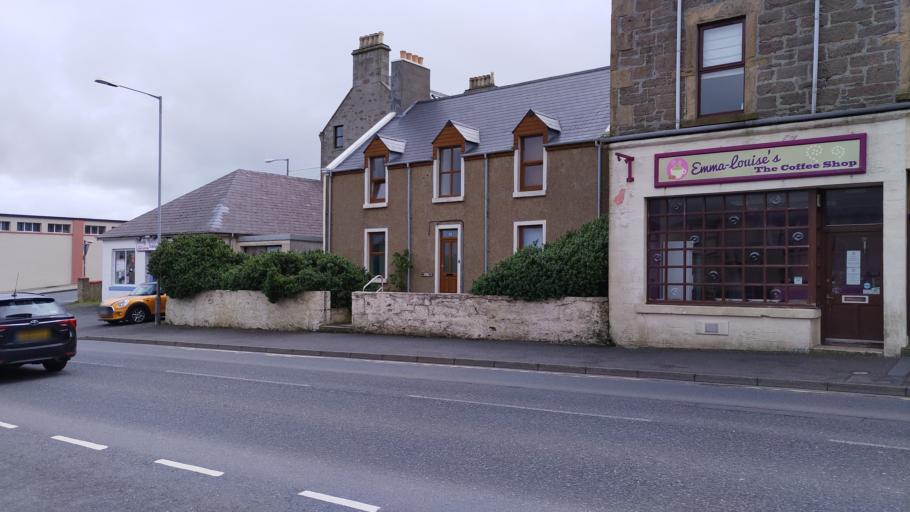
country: GB
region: Scotland
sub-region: Shetland Islands
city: Shetland
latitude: 60.1574
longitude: -1.1484
